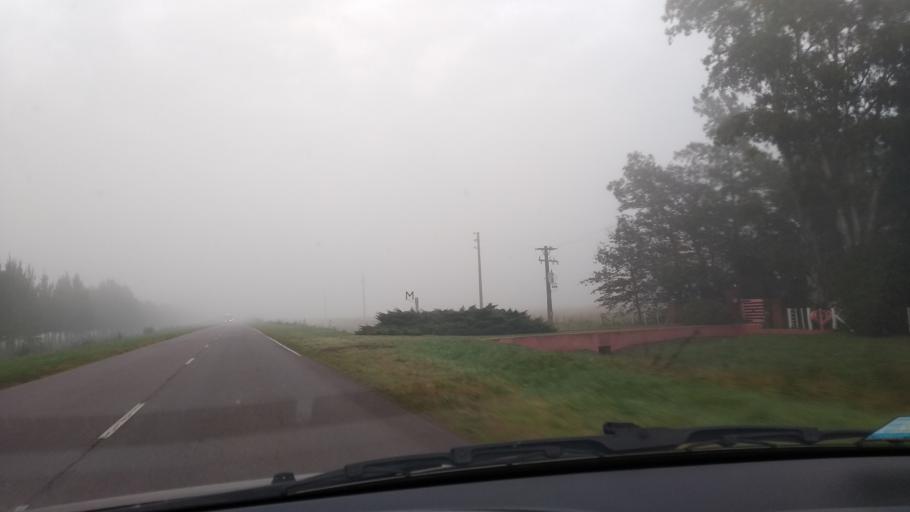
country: AR
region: Buenos Aires
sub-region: Partido de San Vicente
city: San Vicente
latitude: -35.2469
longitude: -58.4877
